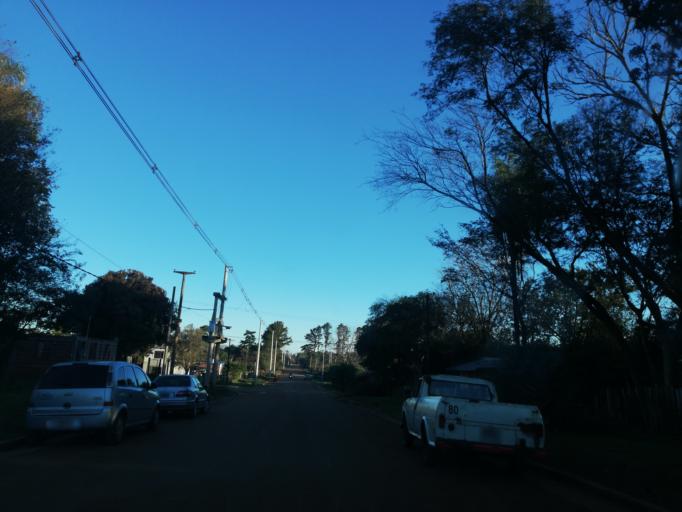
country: AR
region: Misiones
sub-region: Departamento de Candelaria
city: Candelaria
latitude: -27.4631
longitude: -55.7488
